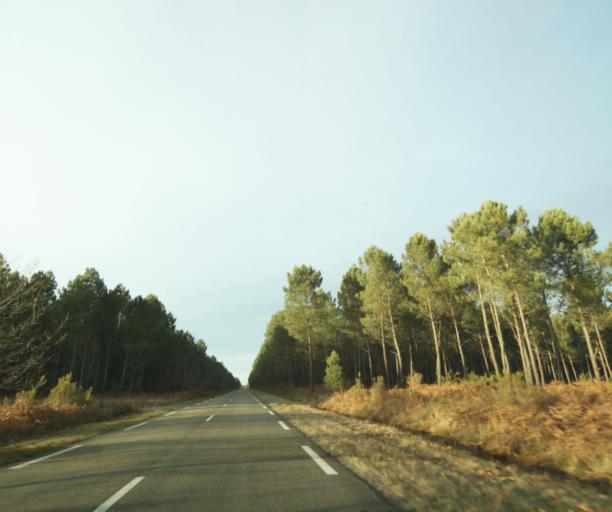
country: FR
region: Aquitaine
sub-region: Departement des Landes
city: Gabarret
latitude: 44.1367
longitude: -0.1180
